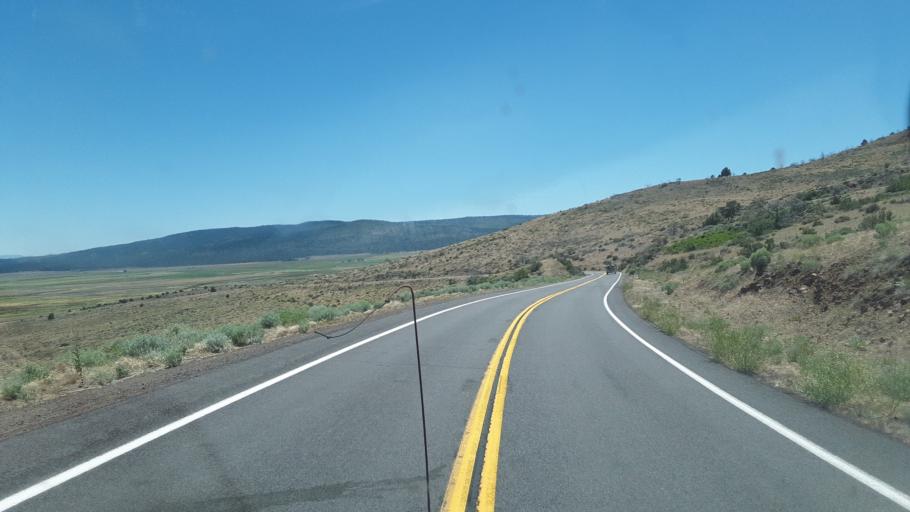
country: US
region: California
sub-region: Lassen County
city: Susanville
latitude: 40.5965
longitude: -120.6432
